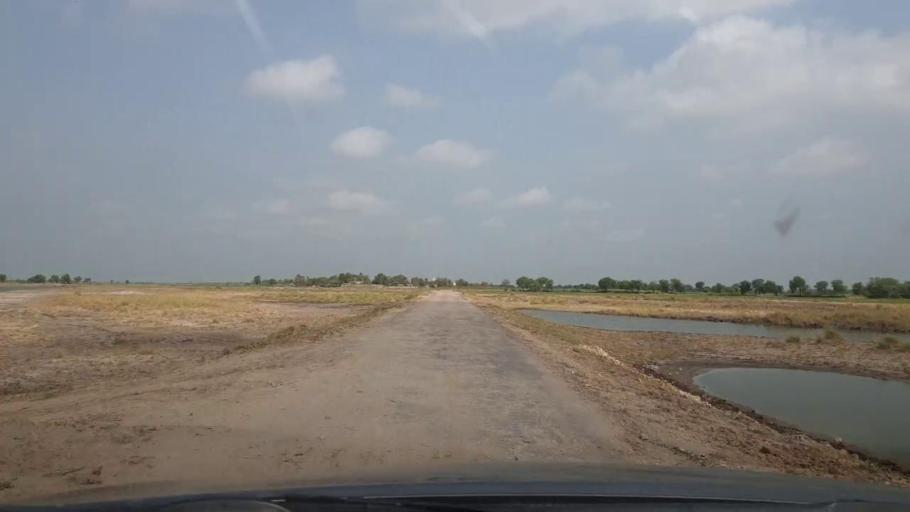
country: PK
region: Sindh
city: Ratodero
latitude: 27.8375
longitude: 68.3011
